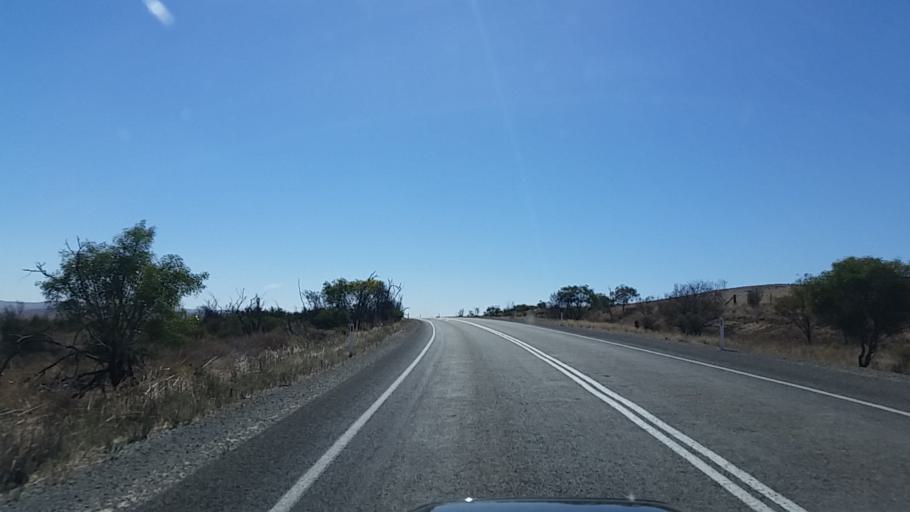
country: AU
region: South Australia
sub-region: Northern Areas
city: Jamestown
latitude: -33.3281
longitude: 138.8884
